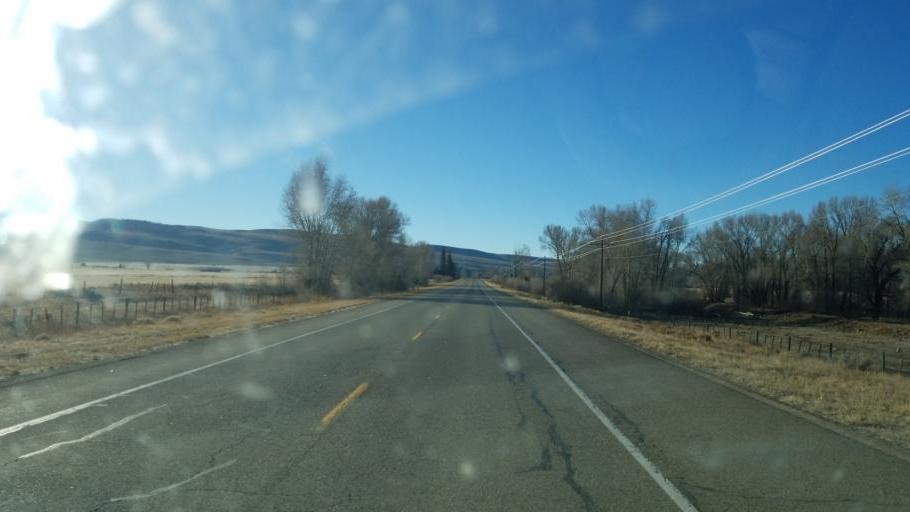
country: US
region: Colorado
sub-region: Gunnison County
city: Crested Butte
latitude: 38.7498
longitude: -106.8594
